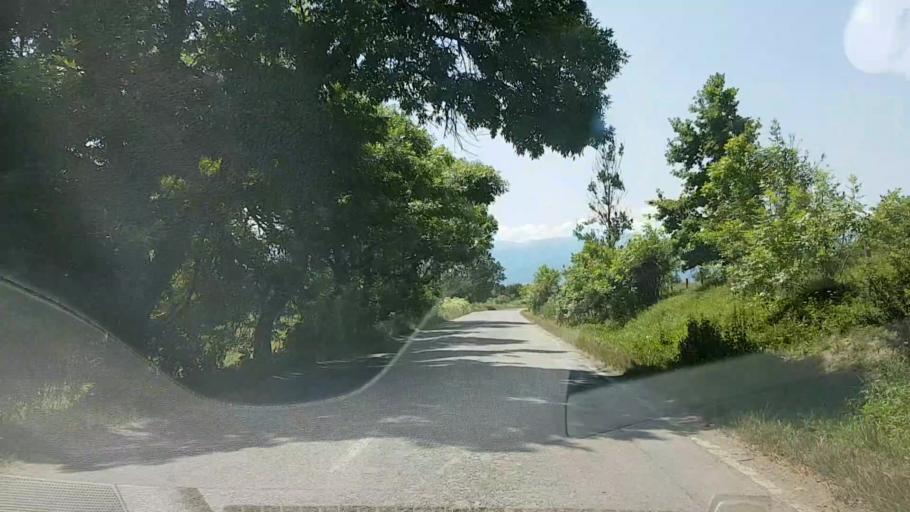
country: RO
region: Brasov
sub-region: Comuna Voila
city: Voila
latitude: 45.8467
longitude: 24.8330
